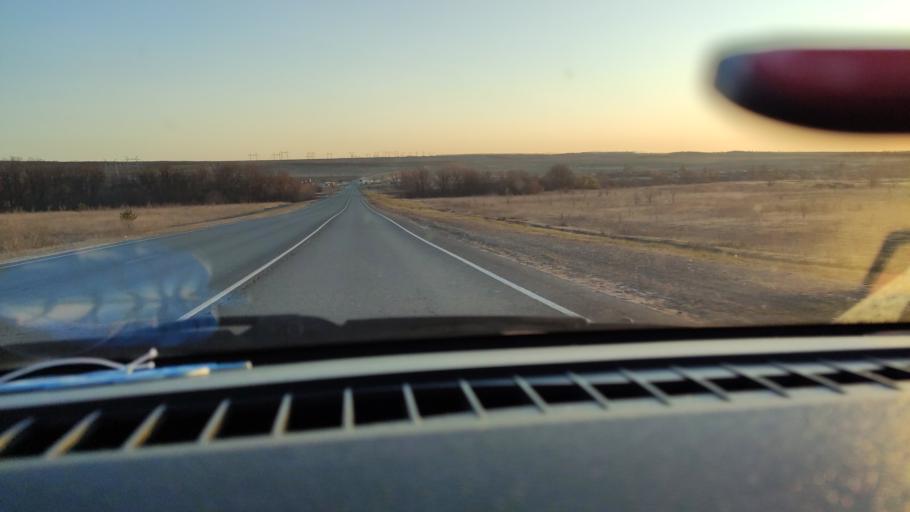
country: RU
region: Saratov
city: Sinodskoye
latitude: 51.9166
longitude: 46.5581
